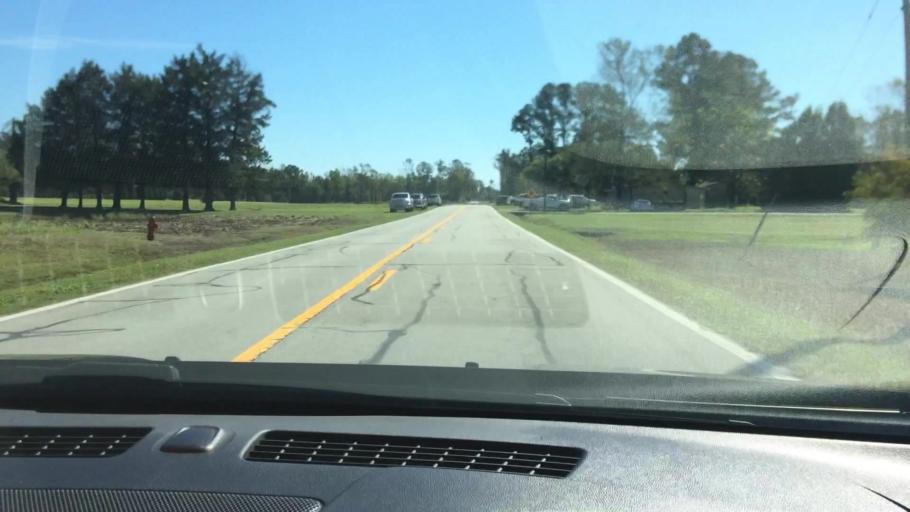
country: US
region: North Carolina
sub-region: Craven County
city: Vanceboro
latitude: 35.3237
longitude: -77.2955
